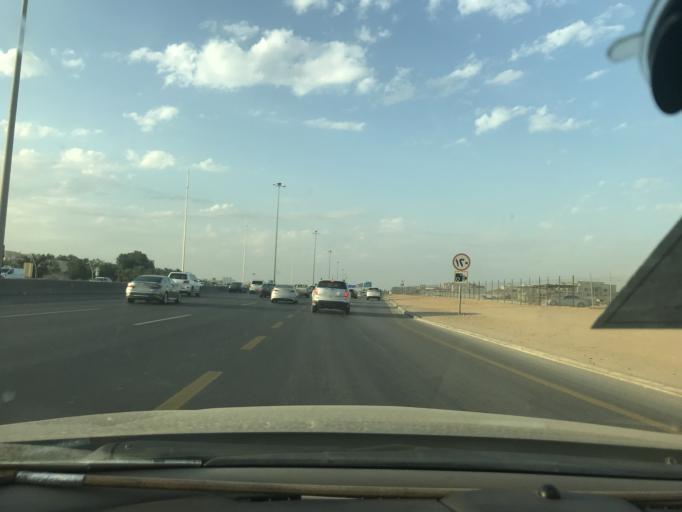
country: SA
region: Ar Riyad
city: Riyadh
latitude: 24.7435
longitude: 46.5863
